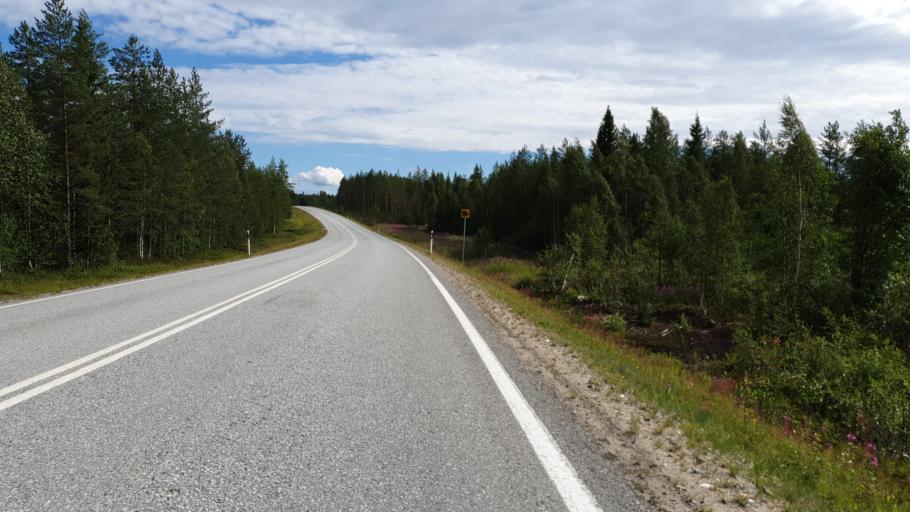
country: FI
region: Kainuu
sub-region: Kehys-Kainuu
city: Kuhmo
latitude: 64.4963
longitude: 29.9089
